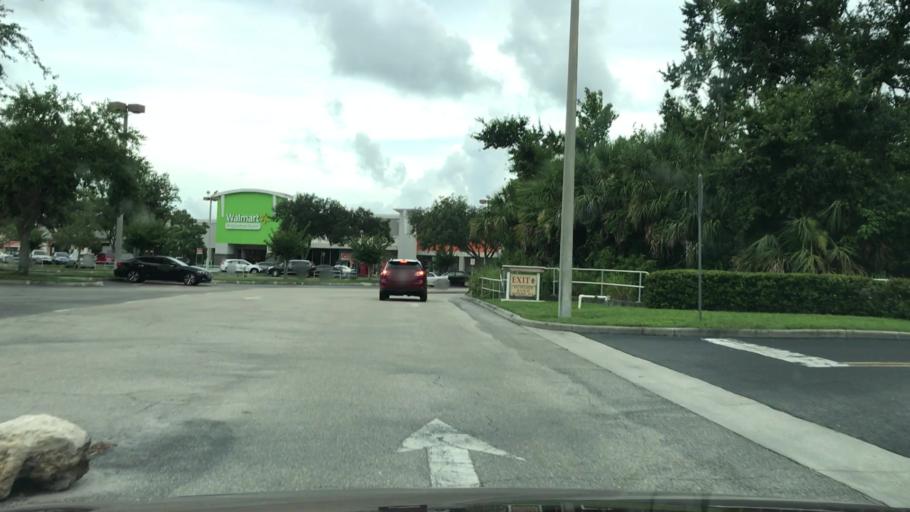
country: US
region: Florida
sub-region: Sarasota County
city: Bee Ridge
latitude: 27.2680
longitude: -82.4634
